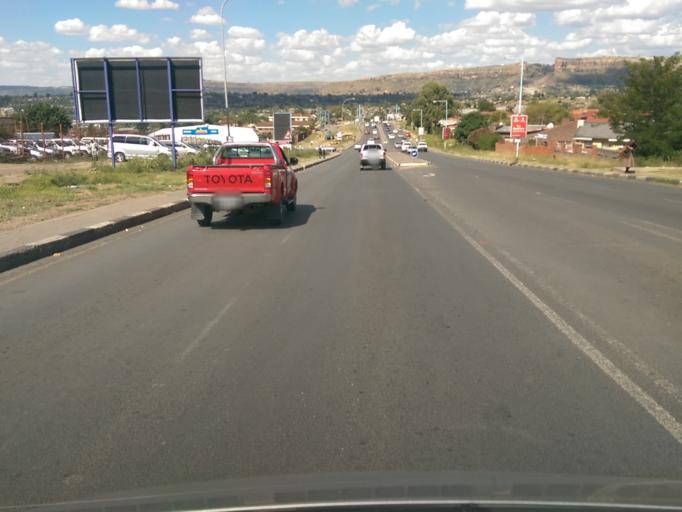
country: LS
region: Maseru
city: Maseru
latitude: -29.3146
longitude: 27.5021
